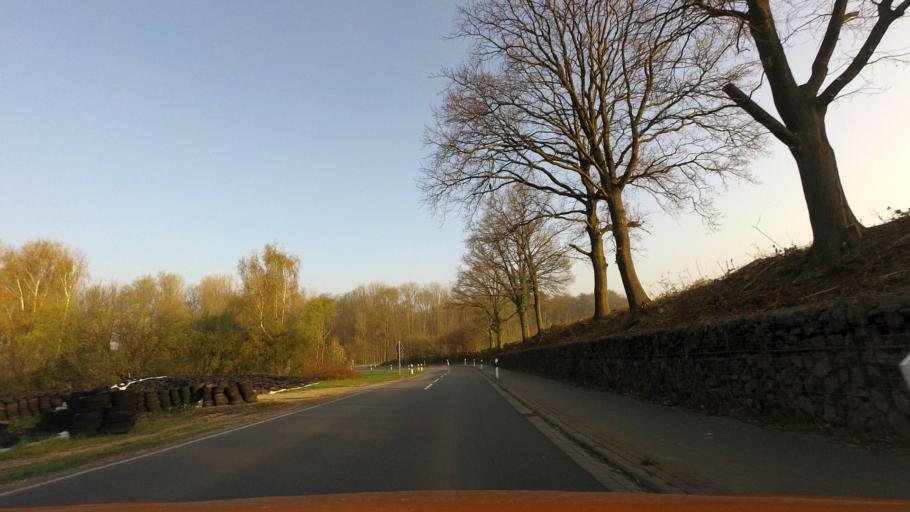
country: DE
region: Lower Saxony
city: Melle
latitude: 52.1865
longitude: 8.3812
